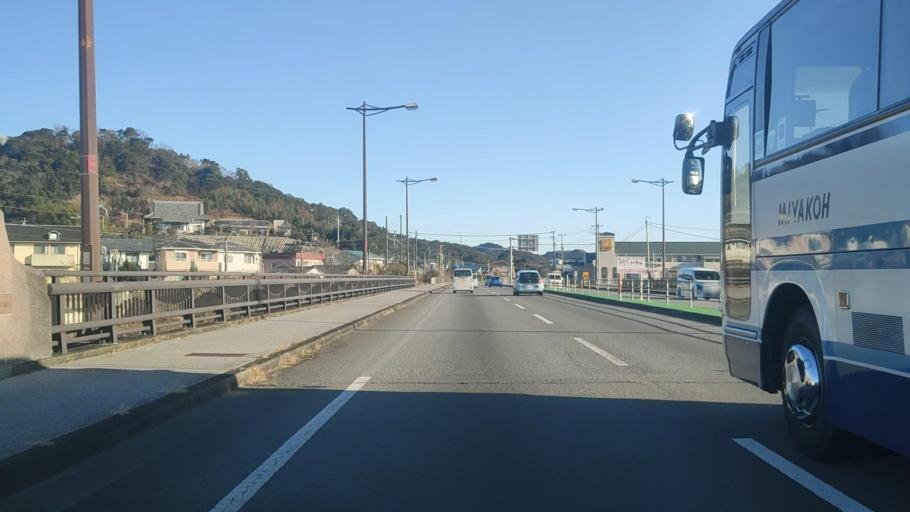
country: JP
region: Miyazaki
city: Nobeoka
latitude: 32.4801
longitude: 131.6565
